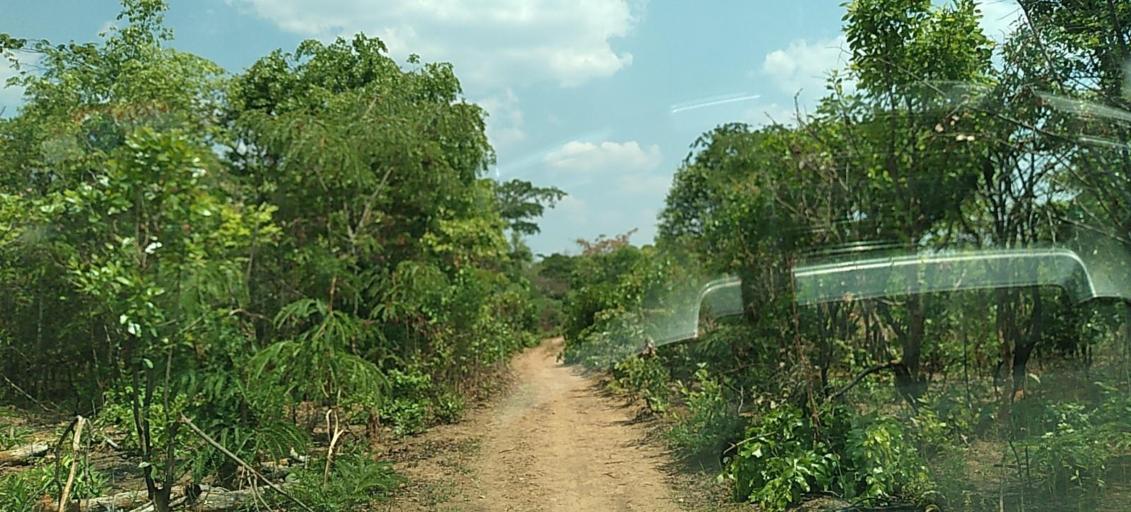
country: CD
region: Katanga
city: Kipushi
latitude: -12.0153
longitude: 27.4338
